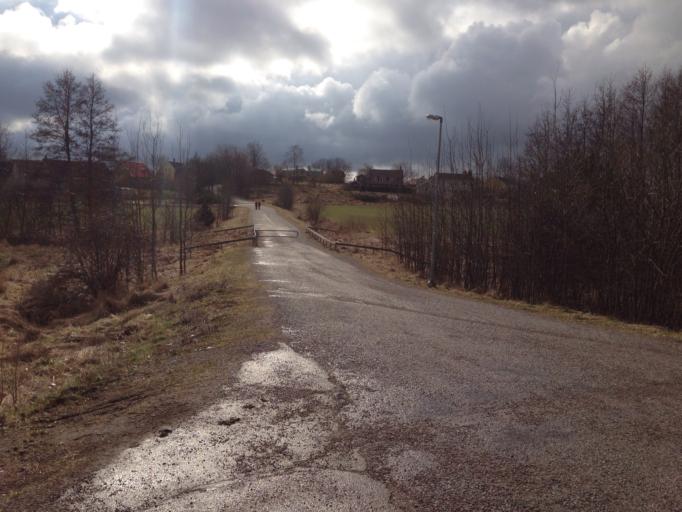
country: SE
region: Uppsala
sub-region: Habo Kommun
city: Balsta
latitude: 59.5538
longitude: 17.5101
